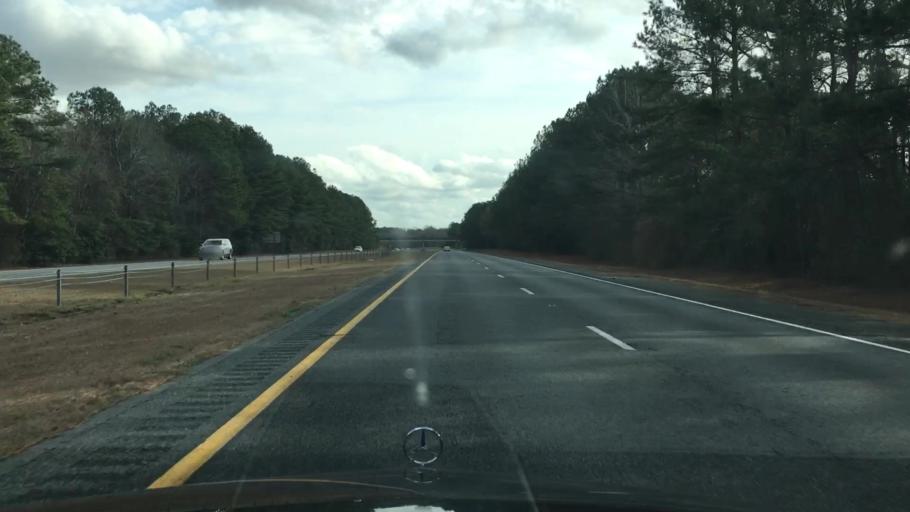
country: US
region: North Carolina
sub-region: Sampson County
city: Clinton
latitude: 35.2175
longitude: -78.3327
